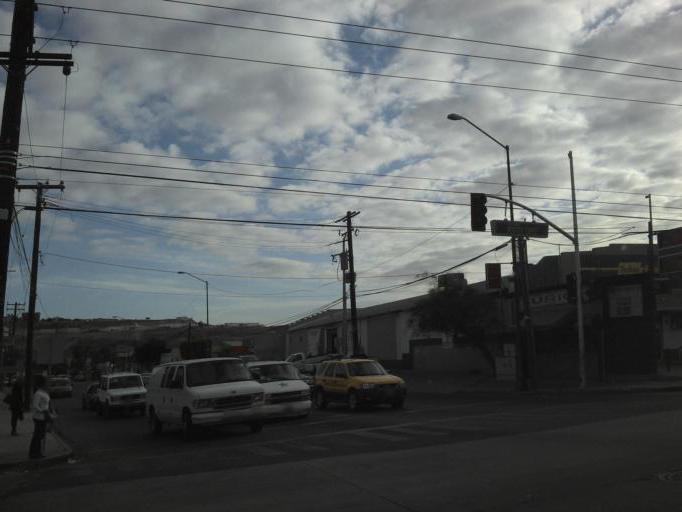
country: MX
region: Baja California
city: Tijuana
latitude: 32.5088
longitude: -116.9726
